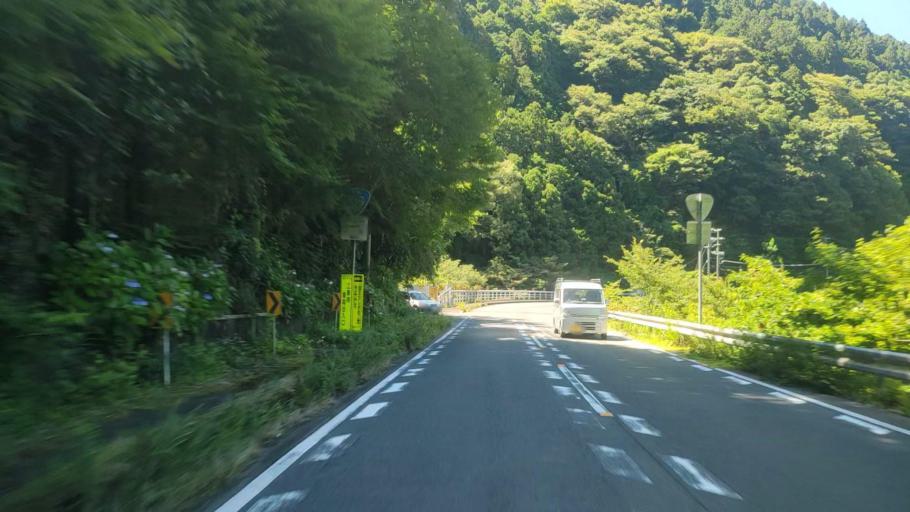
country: JP
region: Nara
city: Yoshino-cho
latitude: 34.3189
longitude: 135.9704
